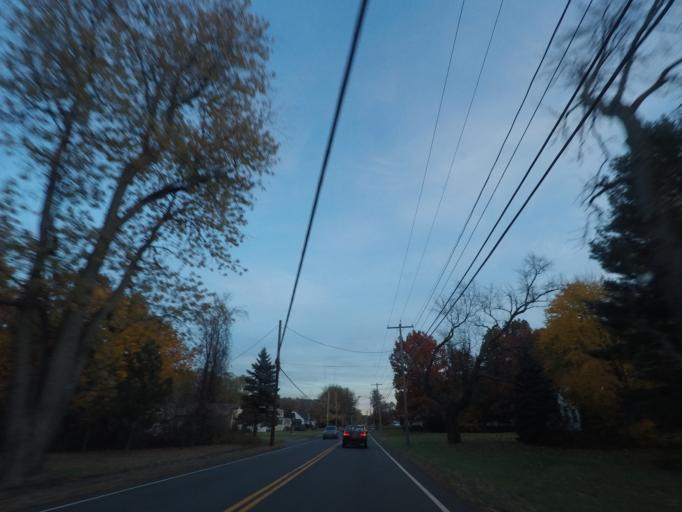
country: US
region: New York
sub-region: Schenectady County
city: Rotterdam
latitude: 42.7698
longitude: -73.9455
